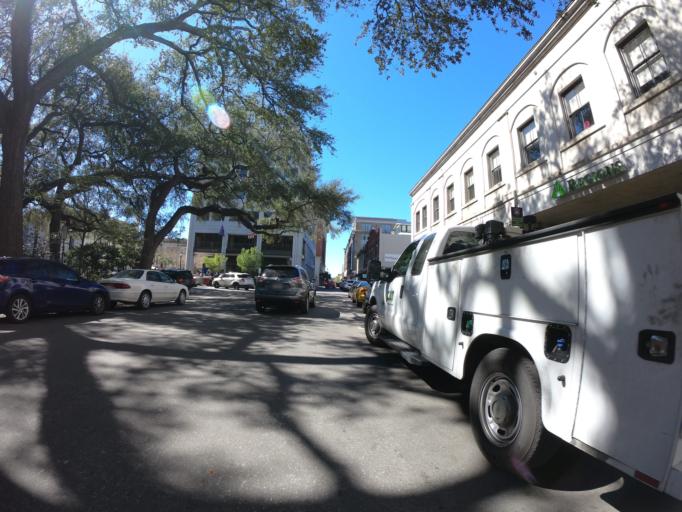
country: US
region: Georgia
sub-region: Chatham County
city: Savannah
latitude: 32.0803
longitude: -81.0917
